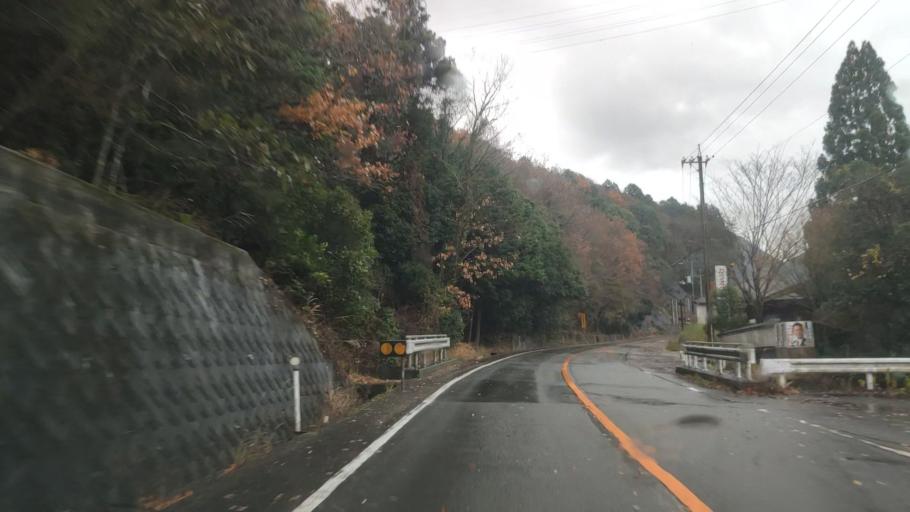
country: JP
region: Tokushima
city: Kamojimacho-jogejima
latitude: 34.1907
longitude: 134.3355
